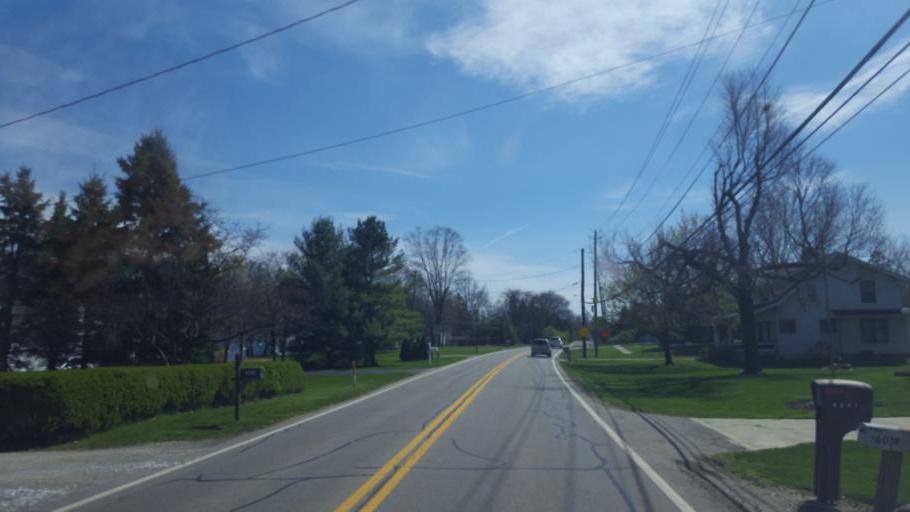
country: US
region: Ohio
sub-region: Franklin County
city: Worthington
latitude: 40.0877
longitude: -83.0495
